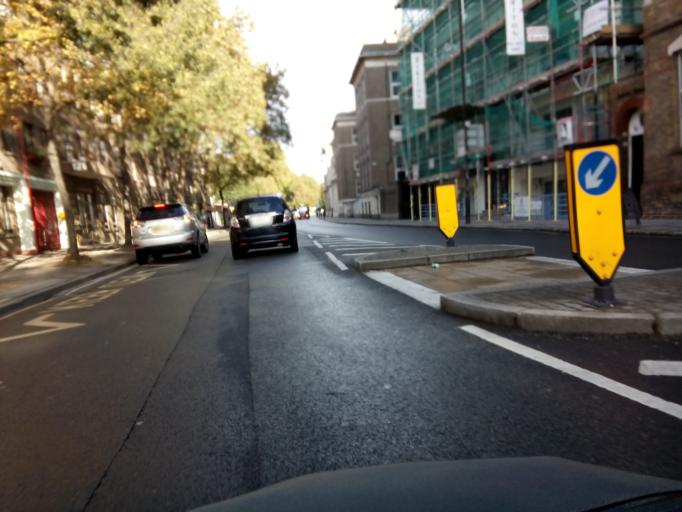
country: GB
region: England
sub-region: Greater London
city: Clerkenwell
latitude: 51.5251
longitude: -0.1168
